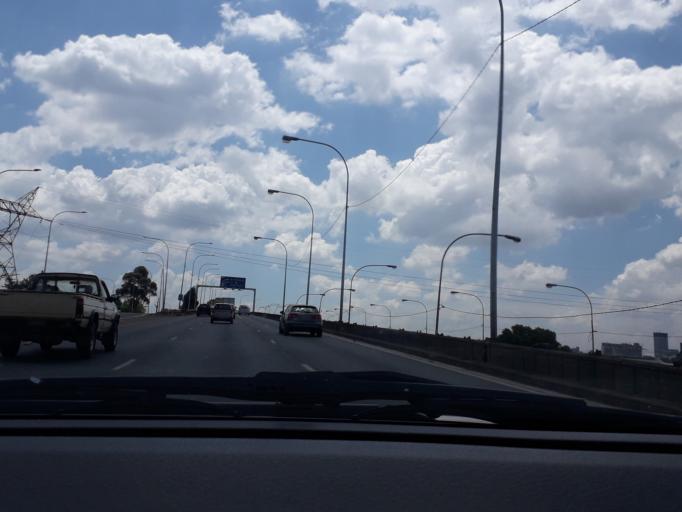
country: ZA
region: Gauteng
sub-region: City of Johannesburg Metropolitan Municipality
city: Johannesburg
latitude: -26.2170
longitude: 28.0234
